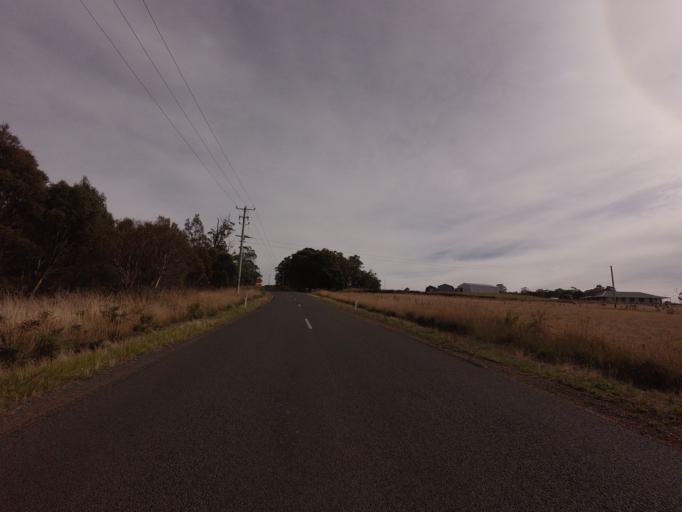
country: AU
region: Tasmania
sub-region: Sorell
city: Sorell
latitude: -42.4111
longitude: 147.4562
